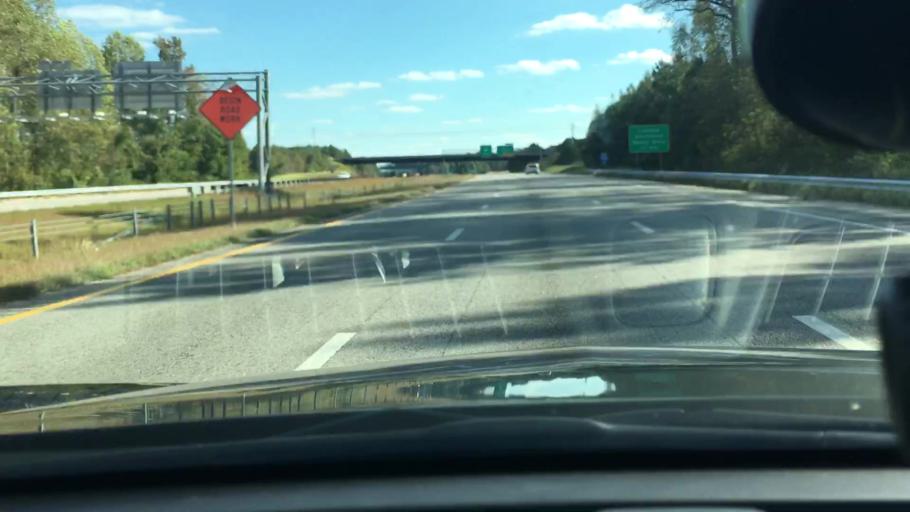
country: US
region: North Carolina
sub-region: Wilson County
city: Lucama
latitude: 35.6896
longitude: -77.9690
